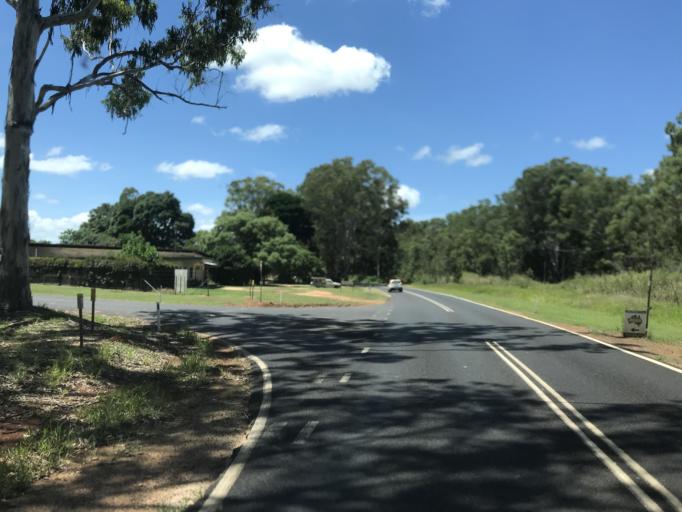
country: AU
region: Queensland
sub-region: Tablelands
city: Atherton
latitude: -17.4264
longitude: 145.3984
